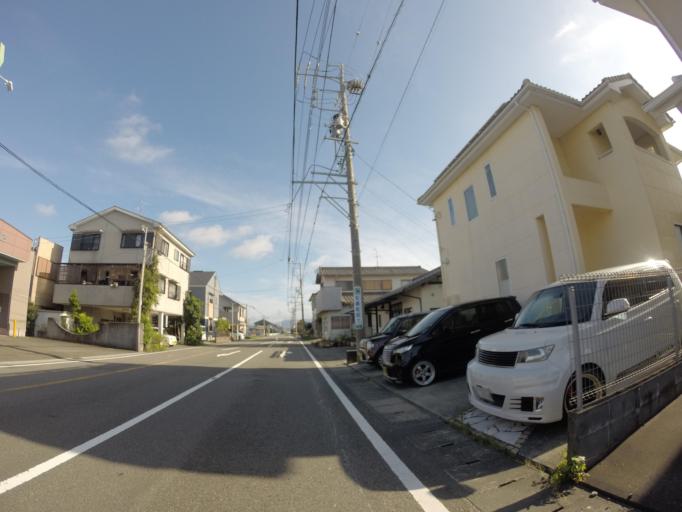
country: JP
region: Shizuoka
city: Yaizu
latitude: 34.8276
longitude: 138.3109
